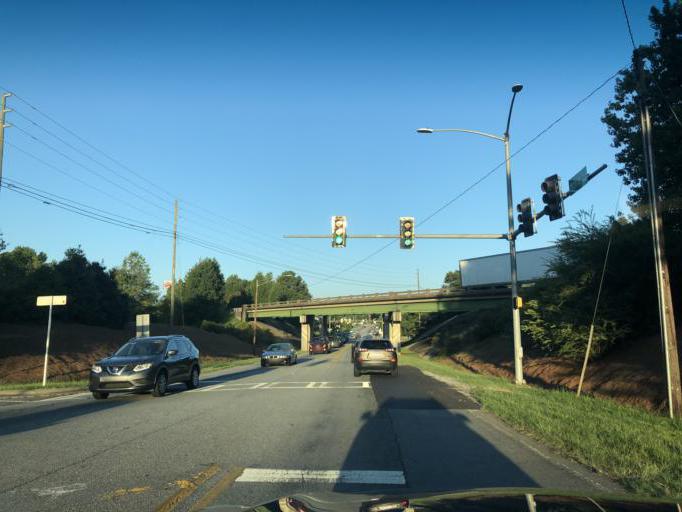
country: US
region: Georgia
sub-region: Muscogee County
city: Columbus
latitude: 32.5224
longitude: -84.8934
